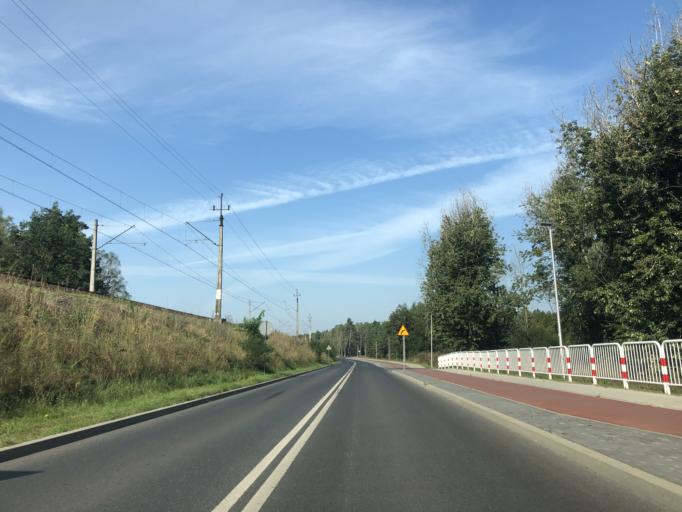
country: PL
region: Greater Poland Voivodeship
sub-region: Powiat pilski
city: Pila
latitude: 53.1333
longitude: 16.7986
